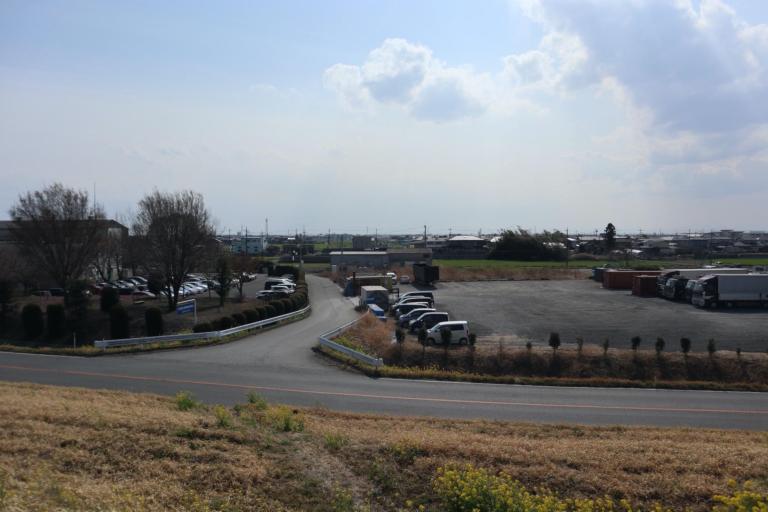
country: JP
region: Tochigi
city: Ashikaga
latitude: 36.3081
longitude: 139.4873
